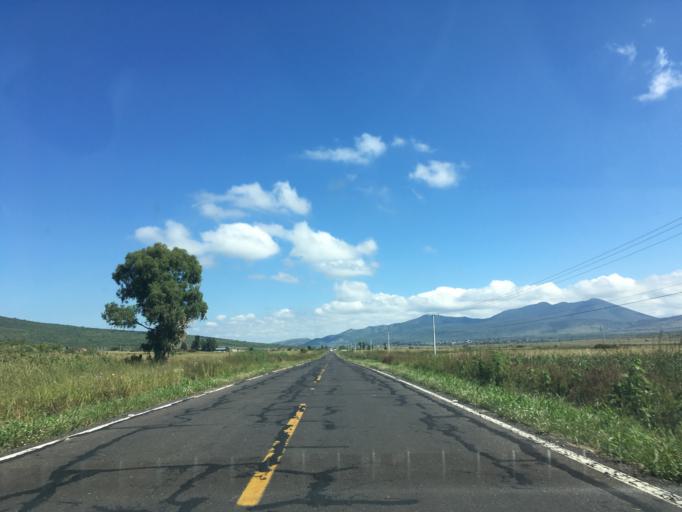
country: MX
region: Mexico
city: Tlazazalca
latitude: 20.0476
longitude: -102.0661
